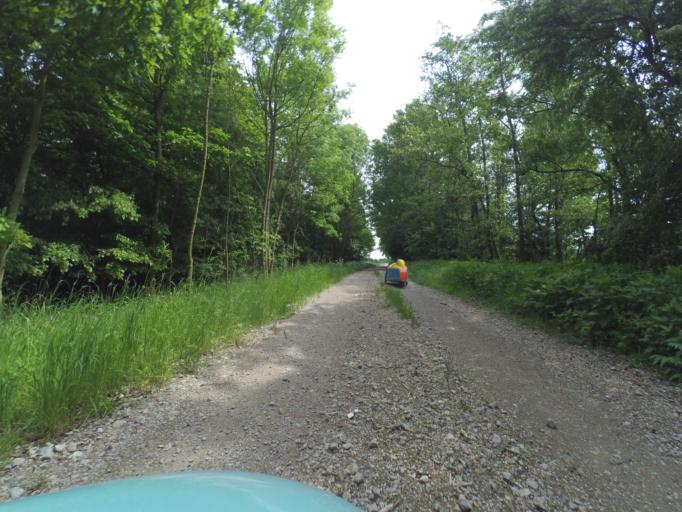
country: DE
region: Lower Saxony
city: Ilsede
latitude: 52.3115
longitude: 10.1384
